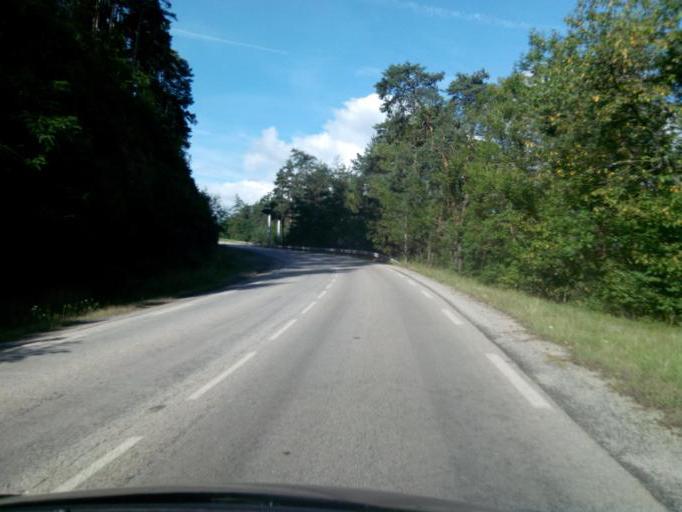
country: FR
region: Auvergne
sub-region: Departement de la Haute-Loire
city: Bas-en-Basset
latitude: 45.2845
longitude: 4.1130
